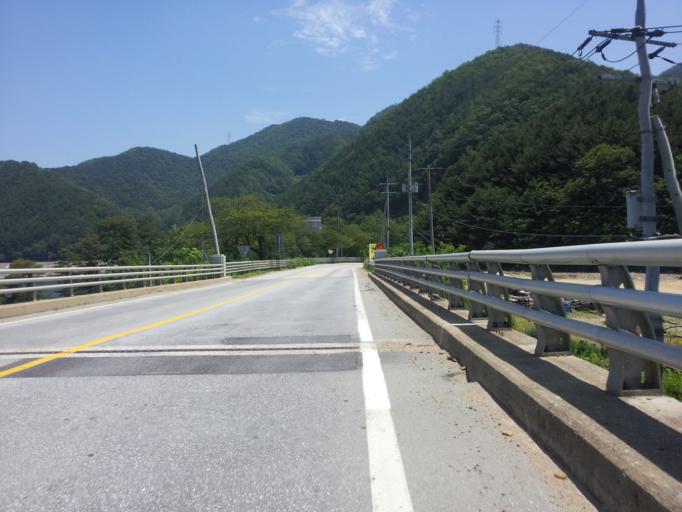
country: KR
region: Chungcheongbuk-do
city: Okcheon
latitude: 36.3702
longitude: 127.6366
